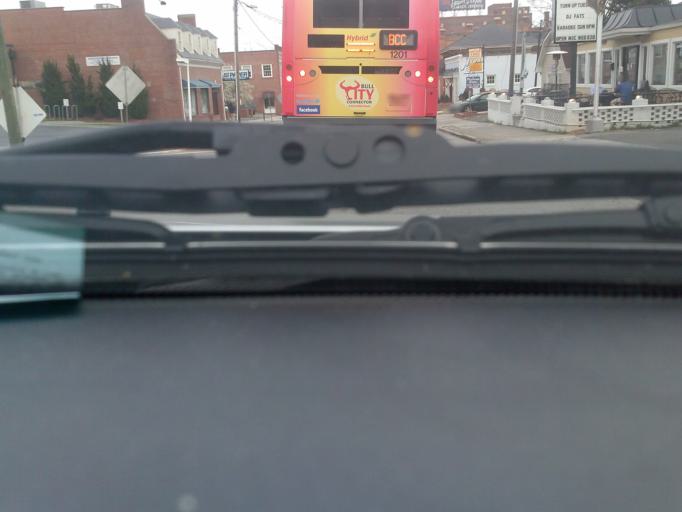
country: US
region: North Carolina
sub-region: Durham County
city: Durham
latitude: 36.0013
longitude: -78.9113
